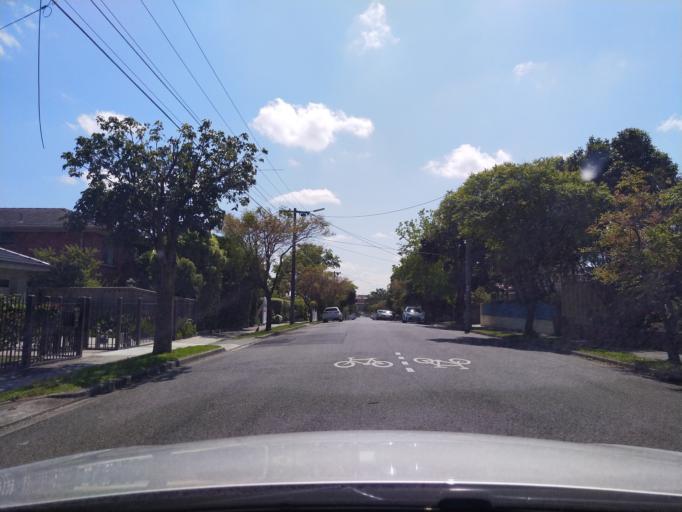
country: AU
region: Victoria
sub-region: Banyule
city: Bellfield
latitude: -37.7631
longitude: 145.0461
